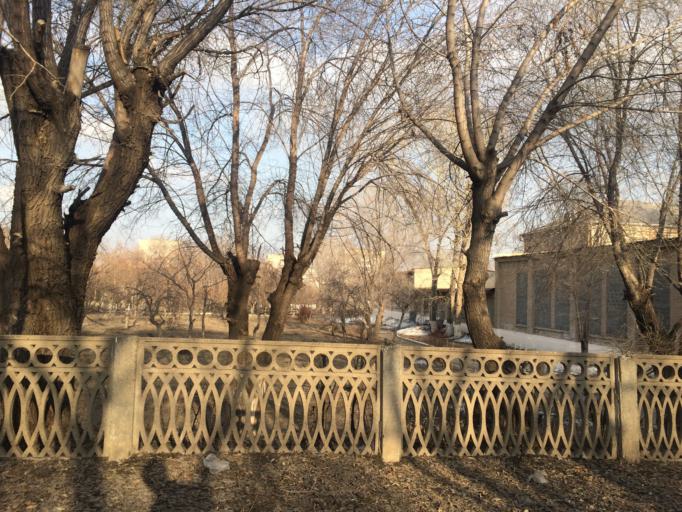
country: RU
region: Chelyabinsk
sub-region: Gorod Magnitogorsk
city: Magnitogorsk
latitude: 53.4014
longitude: 58.9718
